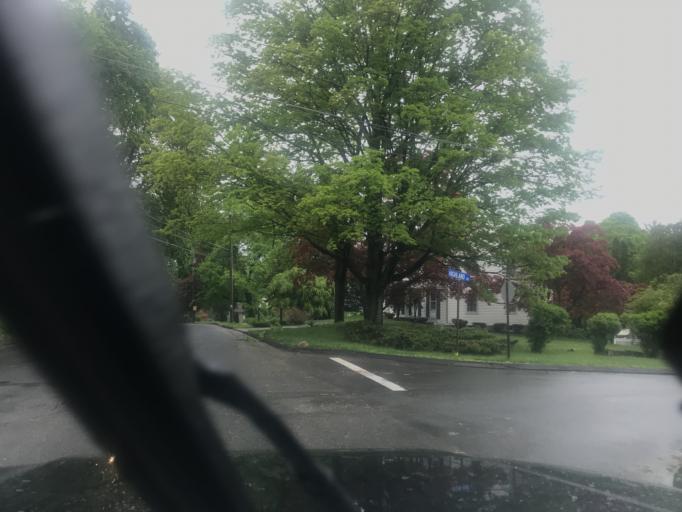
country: US
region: Connecticut
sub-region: Fairfield County
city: Bethel
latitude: 41.3712
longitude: -73.3977
